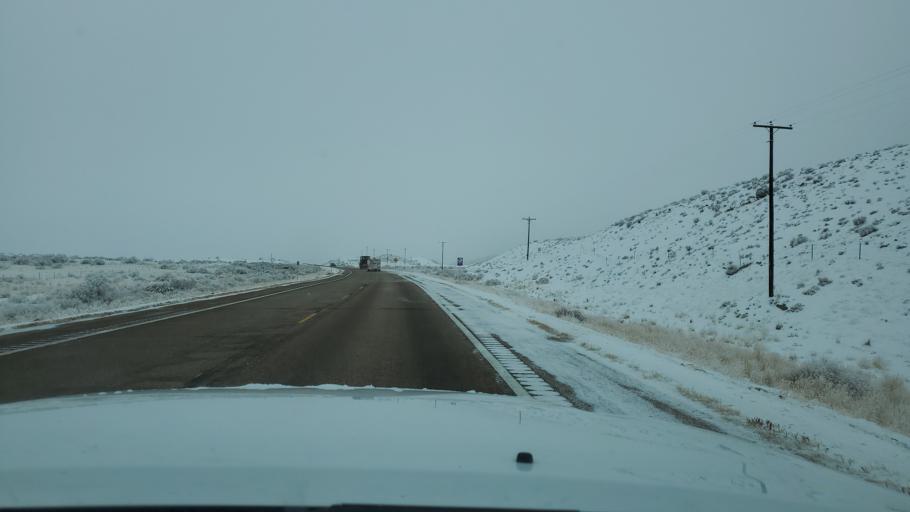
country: US
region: Colorado
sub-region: Rio Blanco County
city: Rangely
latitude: 40.2426
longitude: -108.9497
